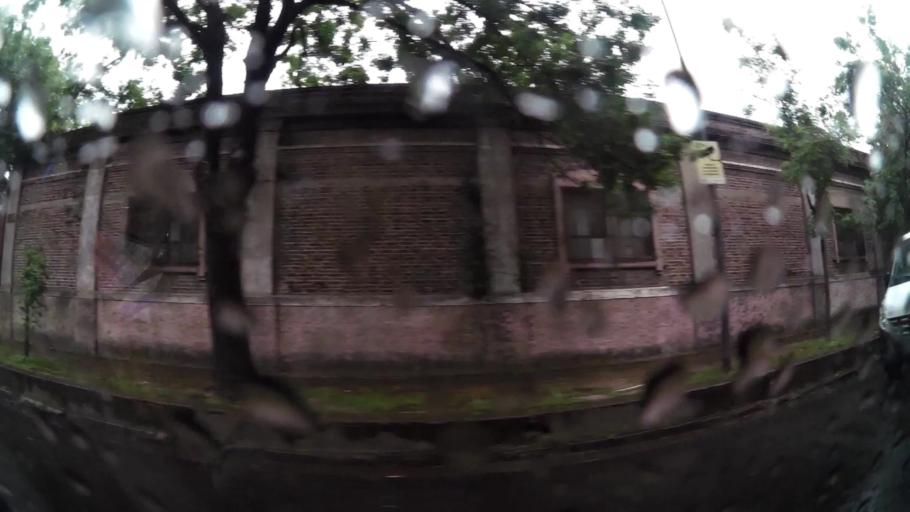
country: AR
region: Buenos Aires
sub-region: Partido de Avellaneda
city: Avellaneda
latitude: -34.6472
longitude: -58.3652
